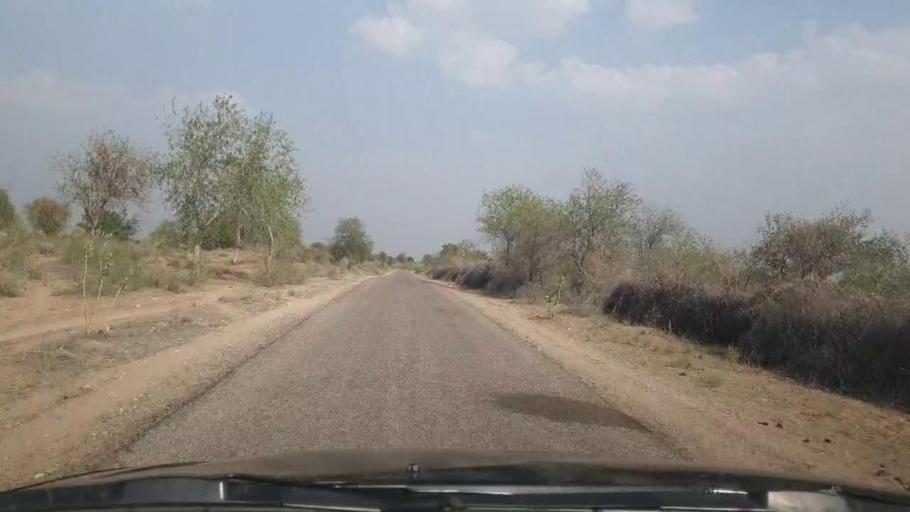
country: PK
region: Sindh
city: Islamkot
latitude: 25.0246
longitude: 70.5635
